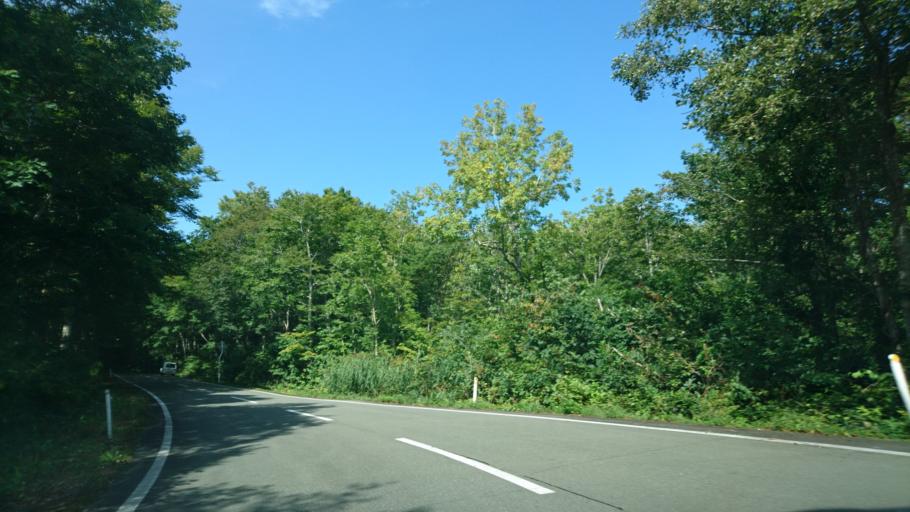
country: JP
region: Akita
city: Yuzawa
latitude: 38.9708
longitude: 140.7130
